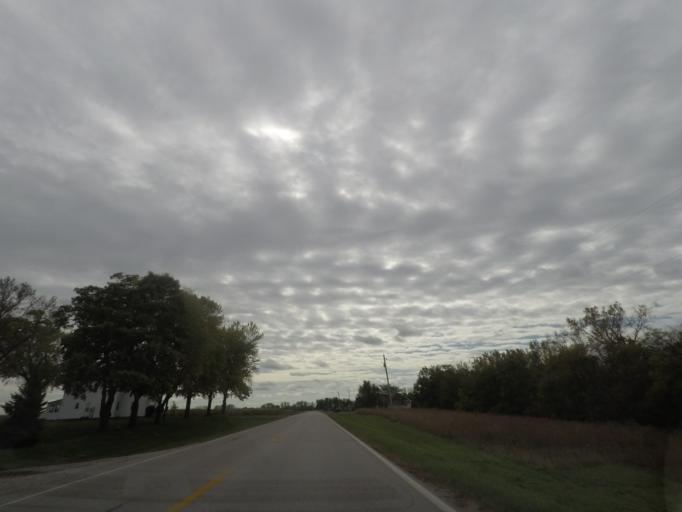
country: US
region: Iowa
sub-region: Story County
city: Huxley
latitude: 41.8433
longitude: -93.5315
